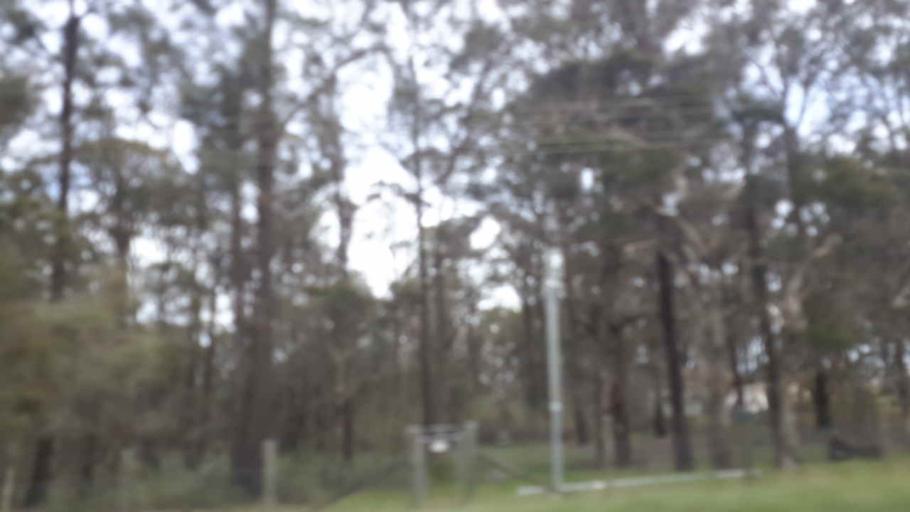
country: AU
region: New South Wales
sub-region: Hawkesbury
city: South Windsor
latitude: -33.6637
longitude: 150.7600
